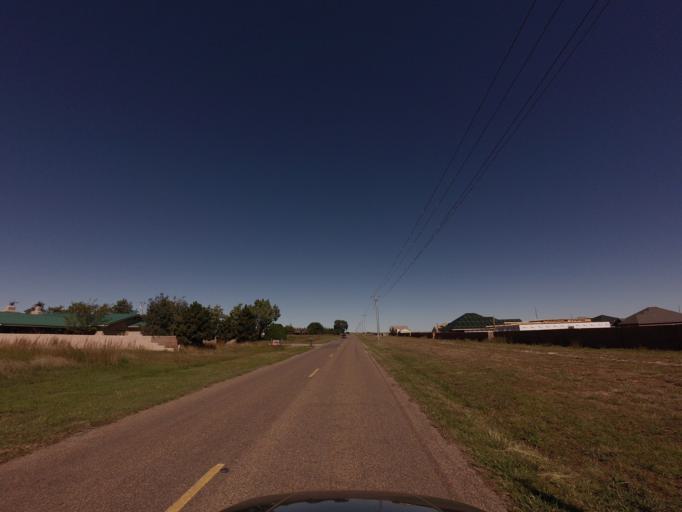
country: US
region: New Mexico
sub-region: Curry County
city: Clovis
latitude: 34.4247
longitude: -103.1608
